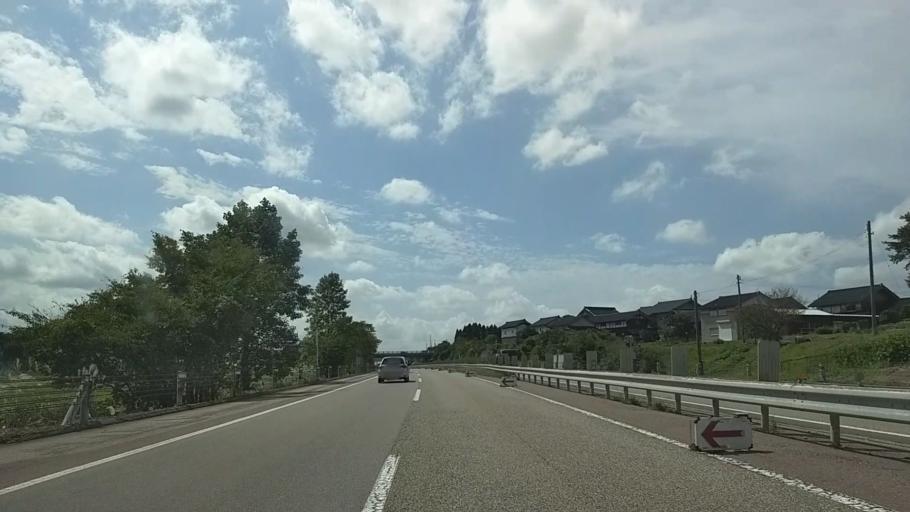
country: JP
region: Toyama
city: Takaoka
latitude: 36.6768
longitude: 137.0364
